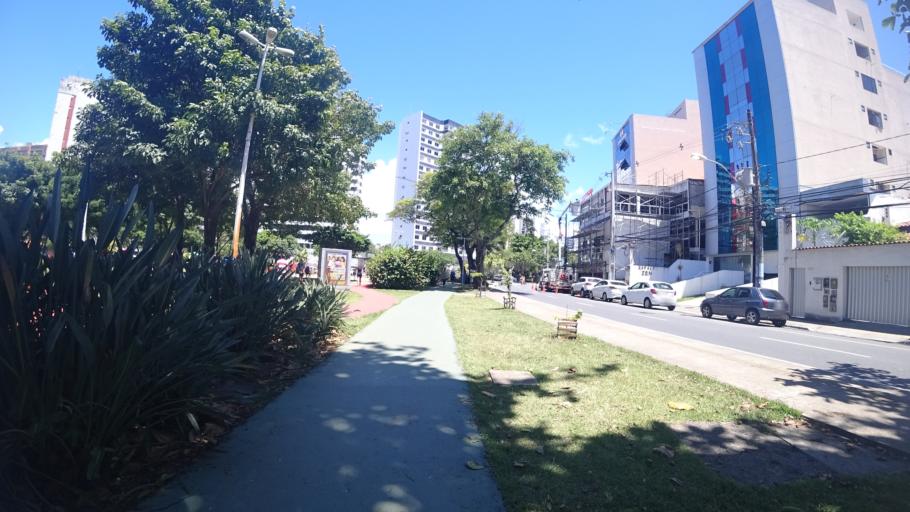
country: BR
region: Bahia
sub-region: Salvador
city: Salvador
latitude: -12.9933
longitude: -38.4610
